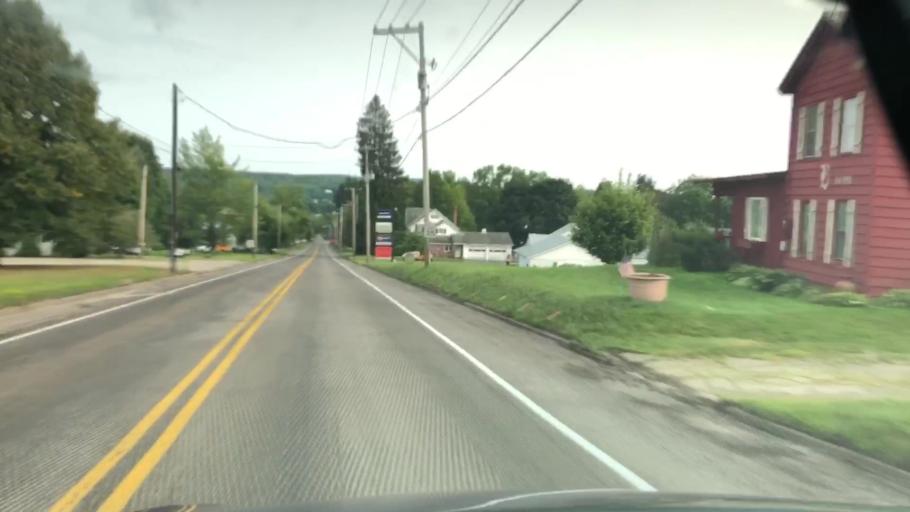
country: US
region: Pennsylvania
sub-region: Crawford County
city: Titusville
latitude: 41.7422
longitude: -79.7654
